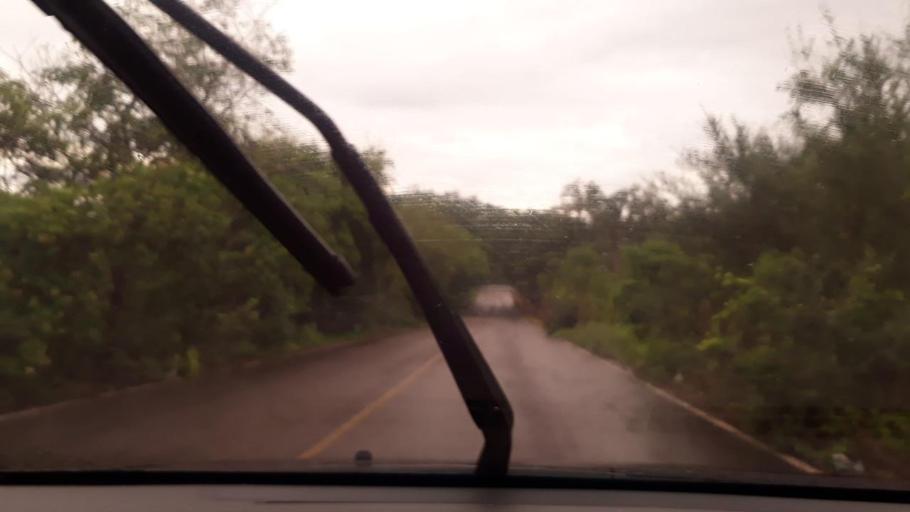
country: GT
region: Jutiapa
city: Comapa
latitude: 14.0447
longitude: -89.9220
